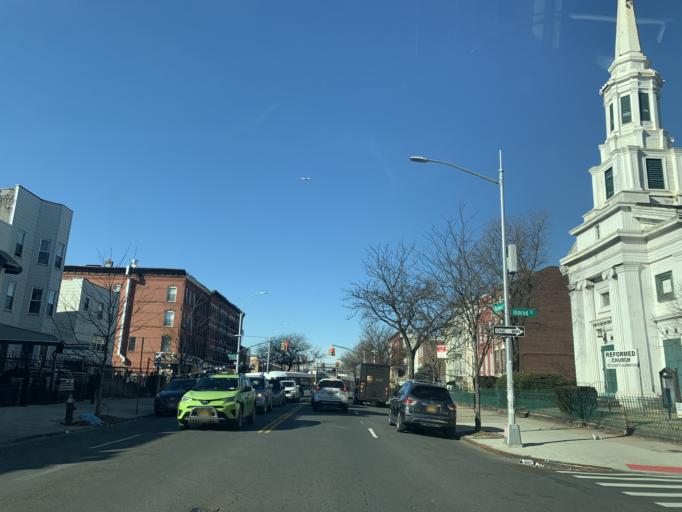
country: US
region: New York
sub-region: Kings County
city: Brooklyn
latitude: 40.6939
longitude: -73.9259
